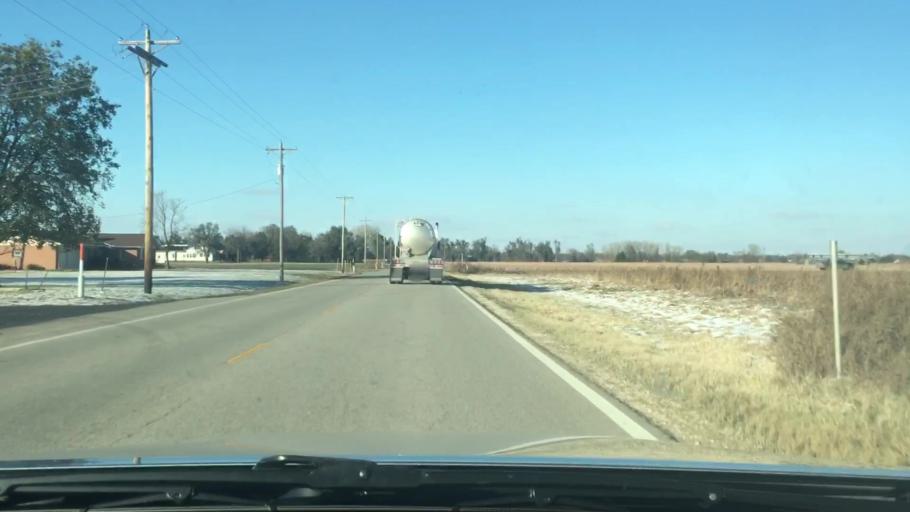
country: US
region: Kansas
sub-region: Rice County
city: Sterling
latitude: 38.1869
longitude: -98.2068
